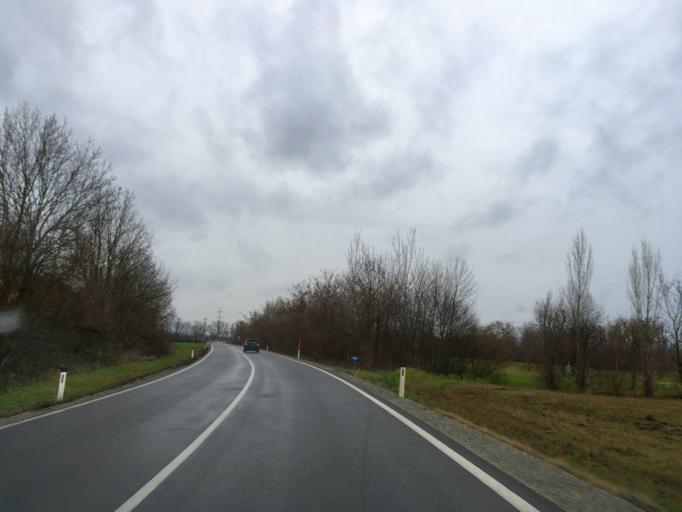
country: AT
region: Lower Austria
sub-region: Politischer Bezirk Wien-Umgebung
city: Ebergassing
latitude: 48.0397
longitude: 16.5381
